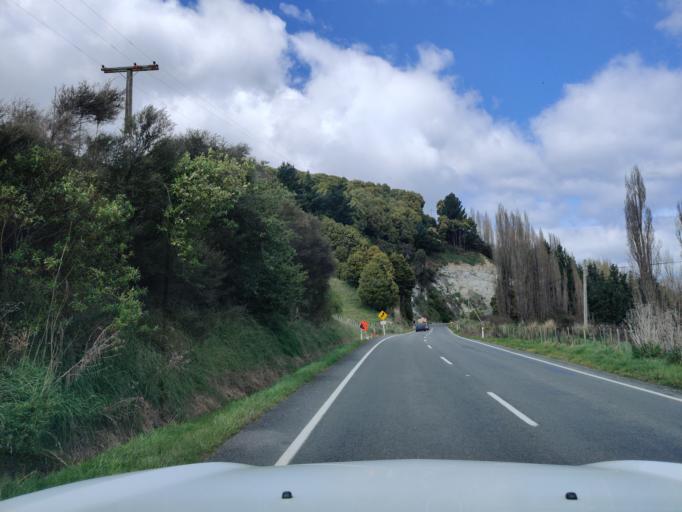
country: NZ
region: Manawatu-Wanganui
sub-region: Ruapehu District
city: Waiouru
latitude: -39.6641
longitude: 175.3334
